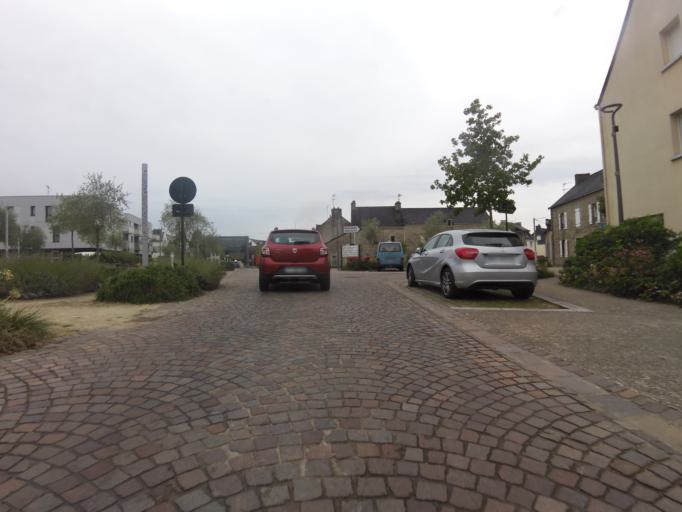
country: FR
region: Brittany
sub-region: Departement du Morbihan
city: Plescop
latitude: 47.6983
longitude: -2.8064
